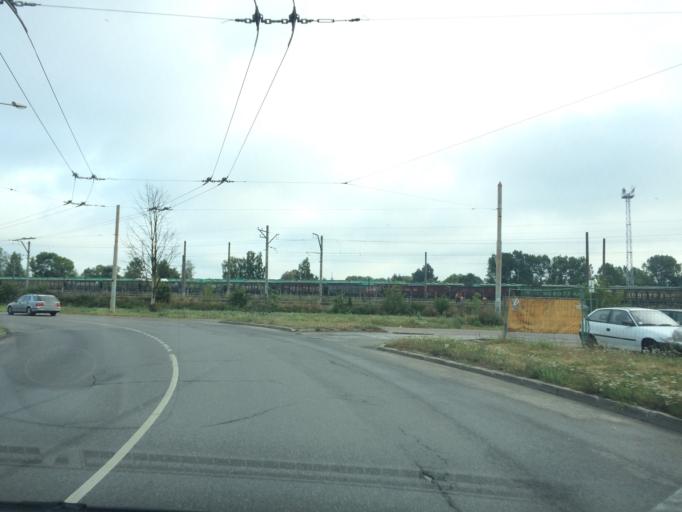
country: LV
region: Kekava
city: Kekava
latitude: 56.9006
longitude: 24.2172
